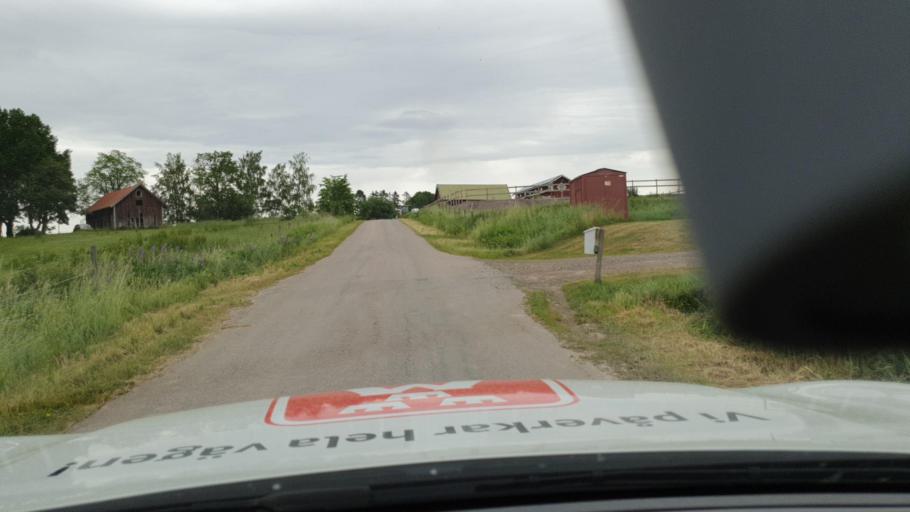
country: SE
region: Vaestra Goetaland
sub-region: Skovde Kommun
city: Skoevde
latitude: 58.3725
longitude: 13.8857
